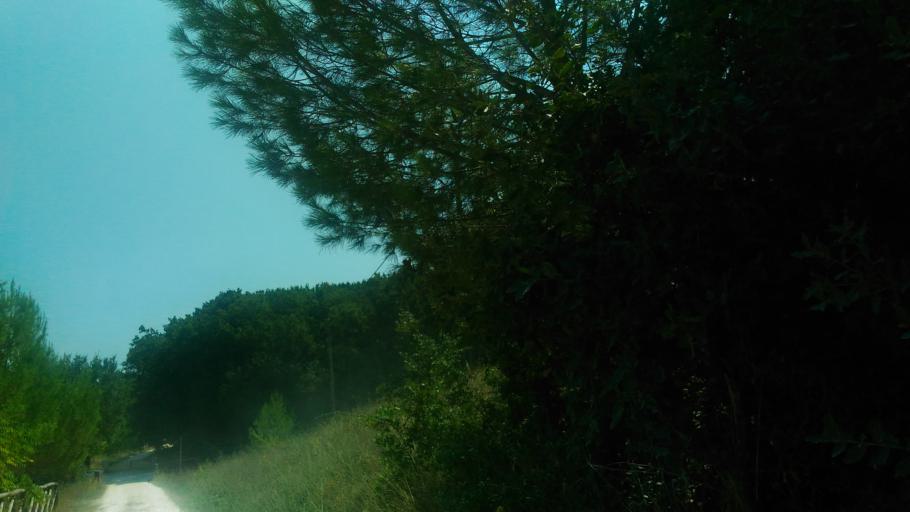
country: IT
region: Apulia
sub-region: Provincia di Brindisi
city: Cisternino
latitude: 40.7308
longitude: 17.3903
